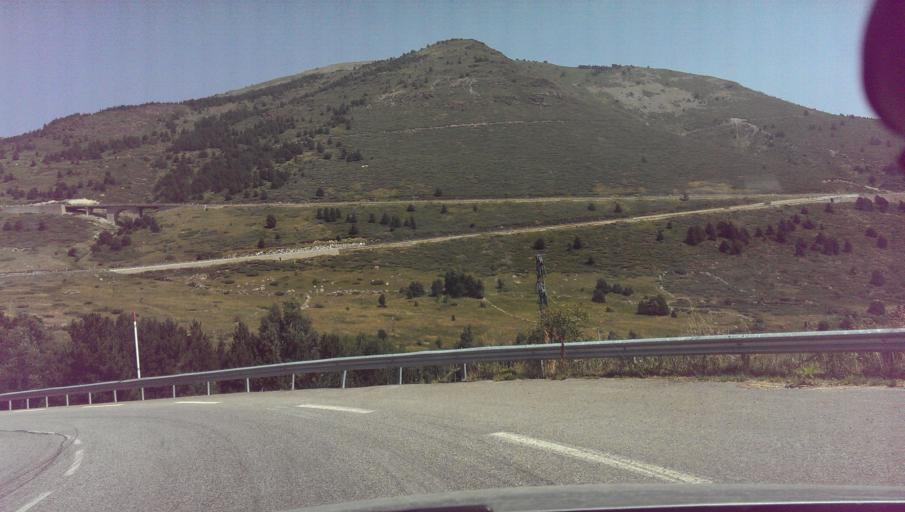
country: AD
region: Encamp
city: Pas de la Casa
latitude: 42.5527
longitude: 1.8165
